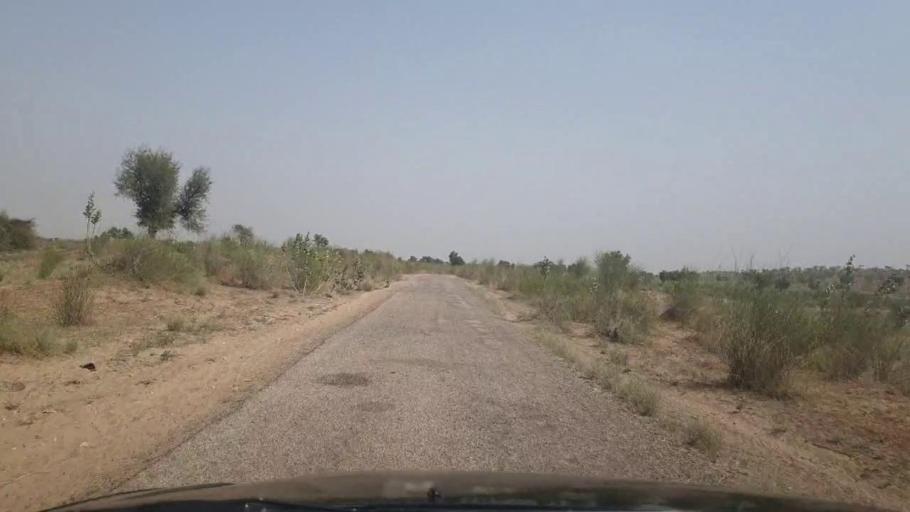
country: PK
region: Sindh
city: Islamkot
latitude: 25.0093
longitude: 70.3904
